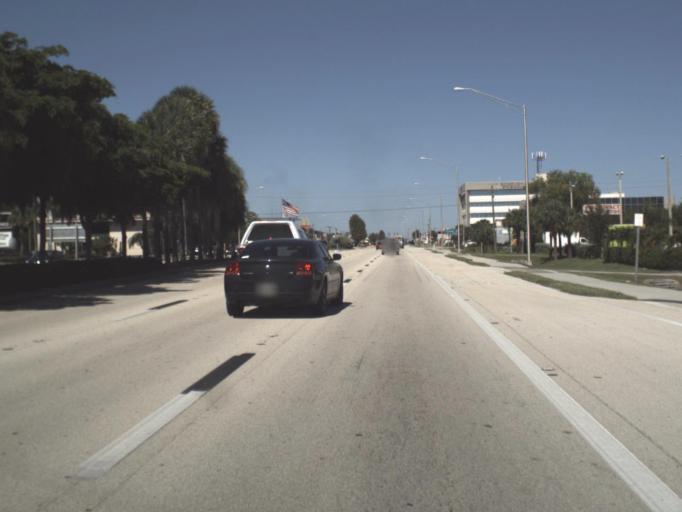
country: US
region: Florida
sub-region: Lee County
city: Villas
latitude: 26.5594
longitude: -81.8717
